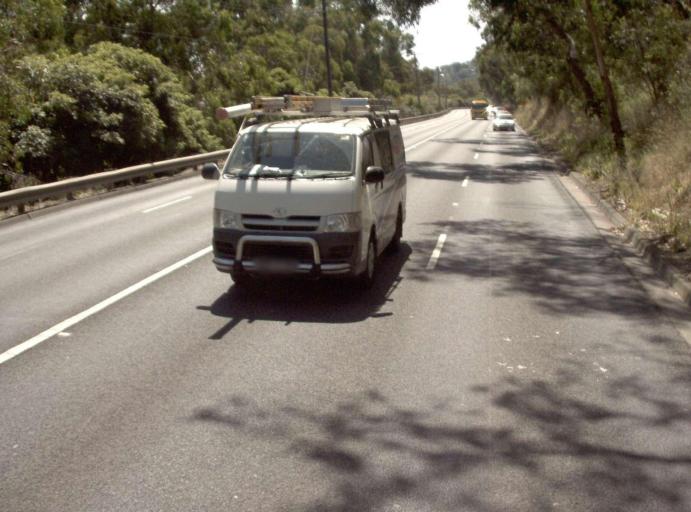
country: AU
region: Victoria
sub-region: Yarra Ranges
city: Tremont
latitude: -37.8988
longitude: 145.3232
